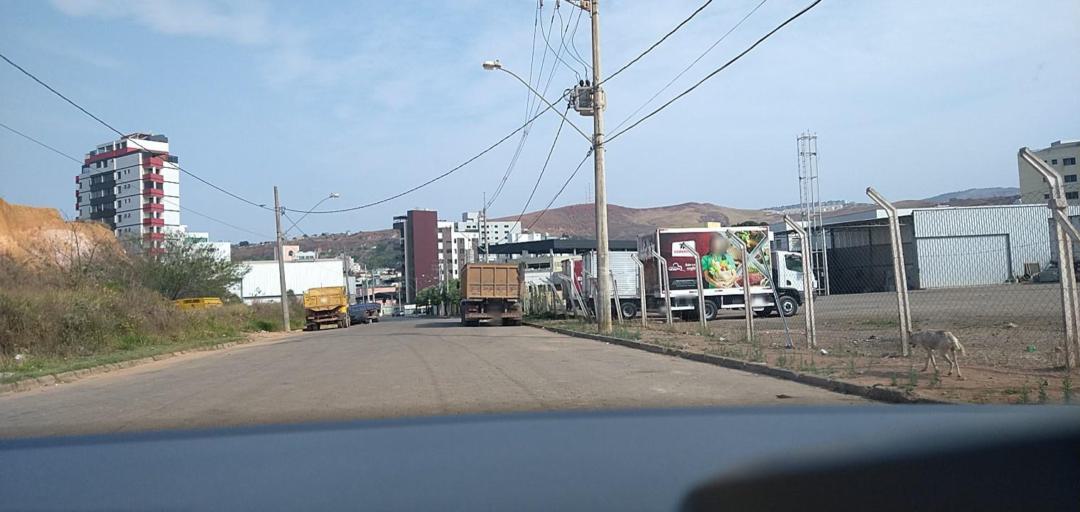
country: BR
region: Minas Gerais
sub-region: Joao Monlevade
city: Joao Monlevade
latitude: -19.8056
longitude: -43.1841
